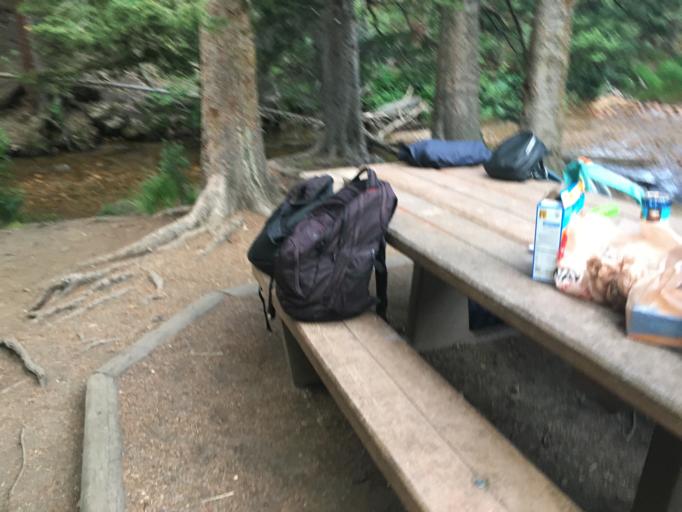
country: US
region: Colorado
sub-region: Larimer County
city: Estes Park
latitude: 40.4133
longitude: -105.6581
